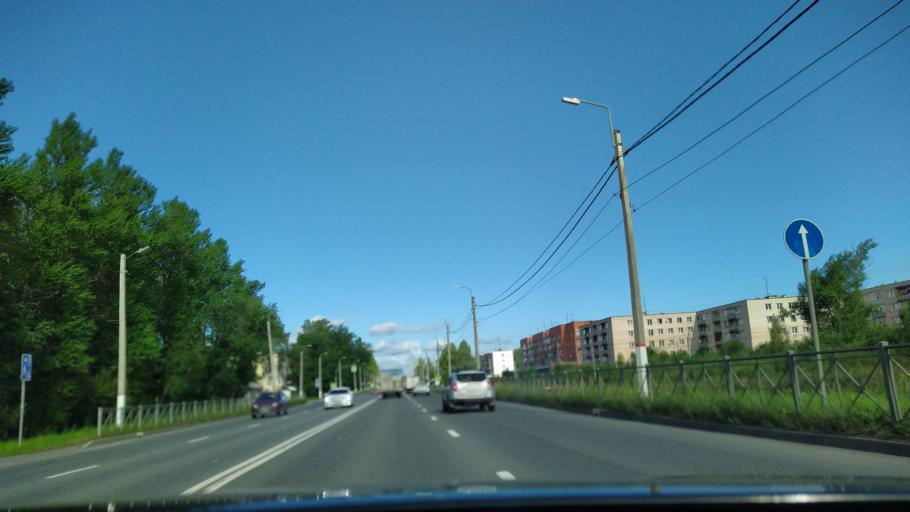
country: RU
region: Leningrad
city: Tosno
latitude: 59.5556
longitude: 30.8503
